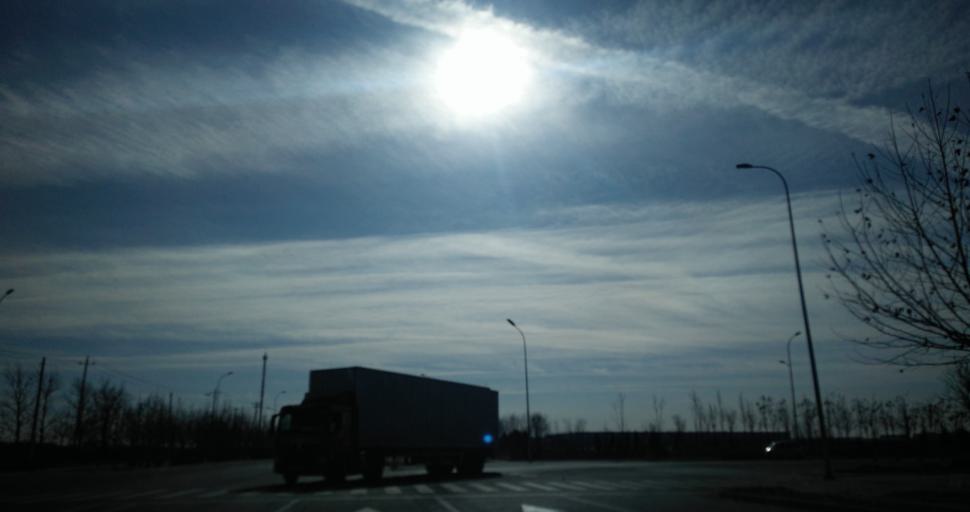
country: CN
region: Beijing
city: Qingyundian
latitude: 39.7325
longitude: 116.5156
